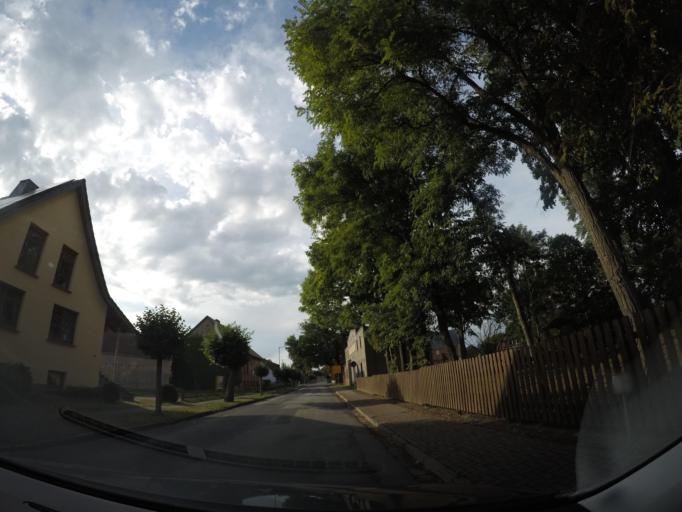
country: DE
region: Saxony-Anhalt
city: Kusey
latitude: 52.5825
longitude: 11.0979
